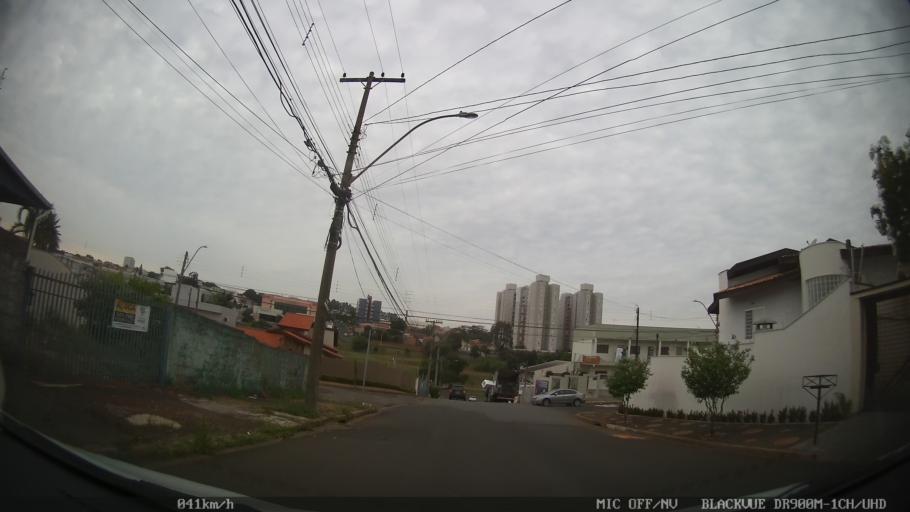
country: BR
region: Sao Paulo
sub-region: Americana
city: Americana
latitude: -22.7384
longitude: -47.3097
